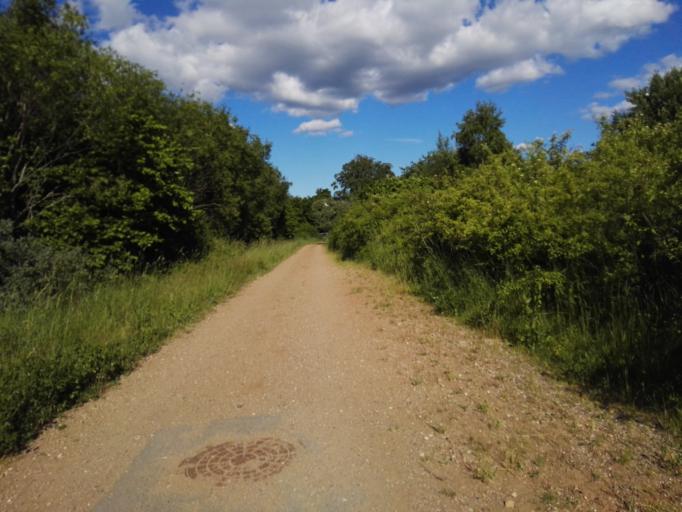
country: DK
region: Capital Region
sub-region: Egedal Kommune
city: Olstykke
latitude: 55.8027
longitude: 12.1668
